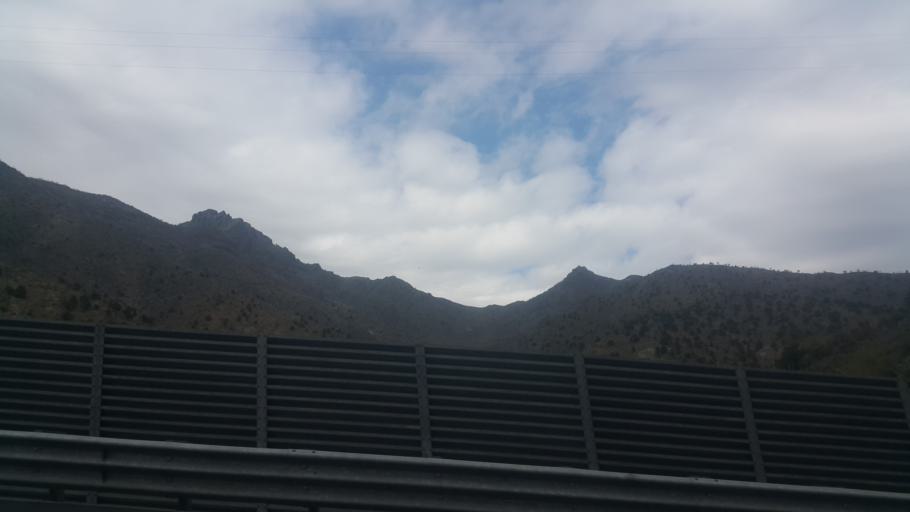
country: TR
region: Nigde
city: Ciftehan
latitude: 37.5460
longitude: 34.7846
